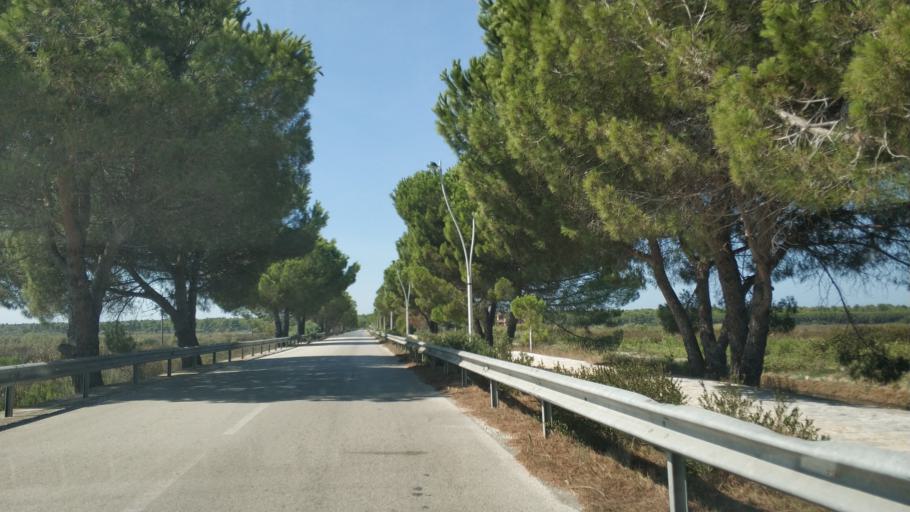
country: AL
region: Fier
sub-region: Rrethi i Lushnjes
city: Divjake
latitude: 40.9914
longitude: 19.5080
